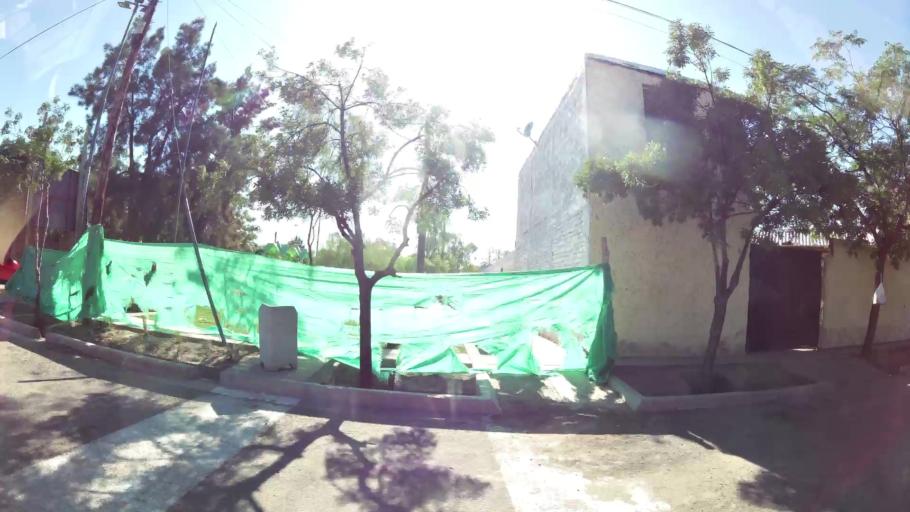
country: AR
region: Mendoza
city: Las Heras
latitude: -32.8728
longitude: -68.8673
